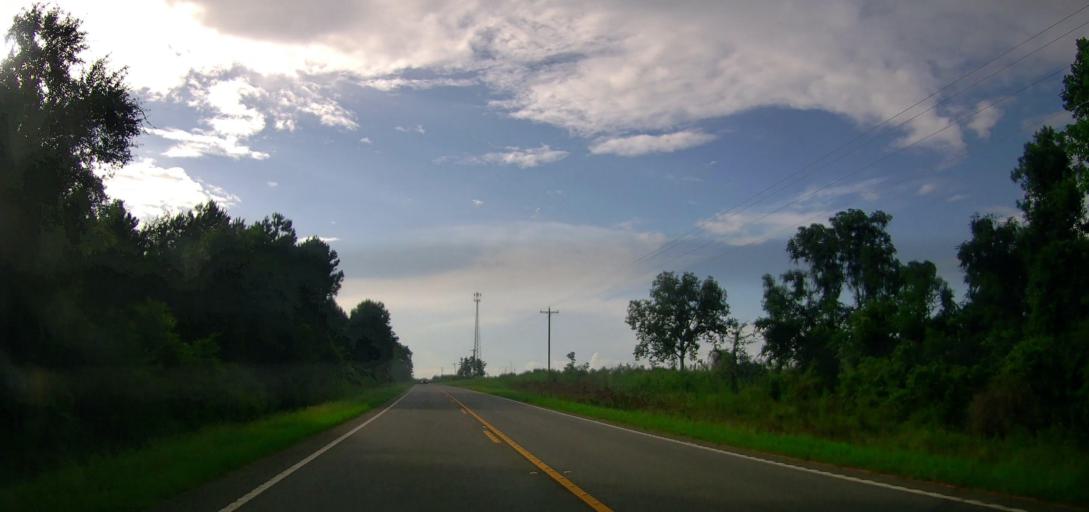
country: US
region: Georgia
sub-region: Coffee County
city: Nicholls
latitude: 31.3253
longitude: -82.5800
